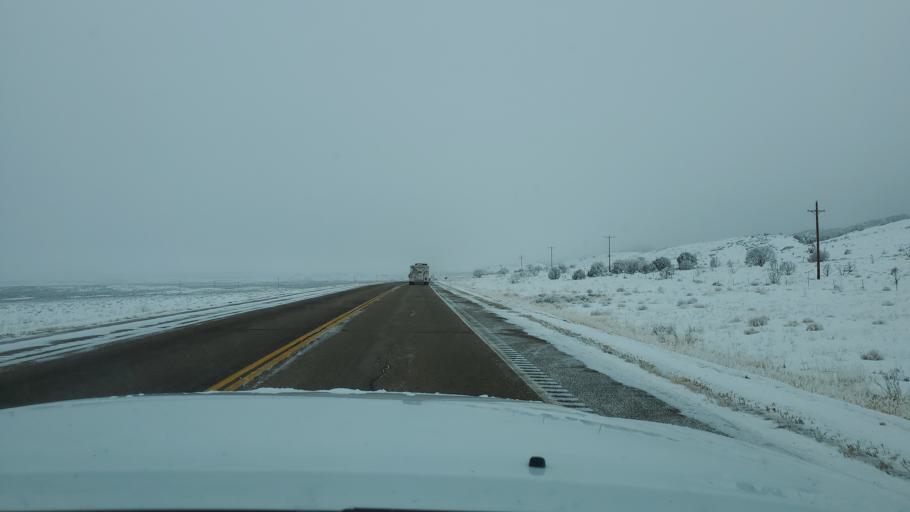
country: US
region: Colorado
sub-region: Rio Blanco County
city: Rangely
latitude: 40.2426
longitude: -108.9592
